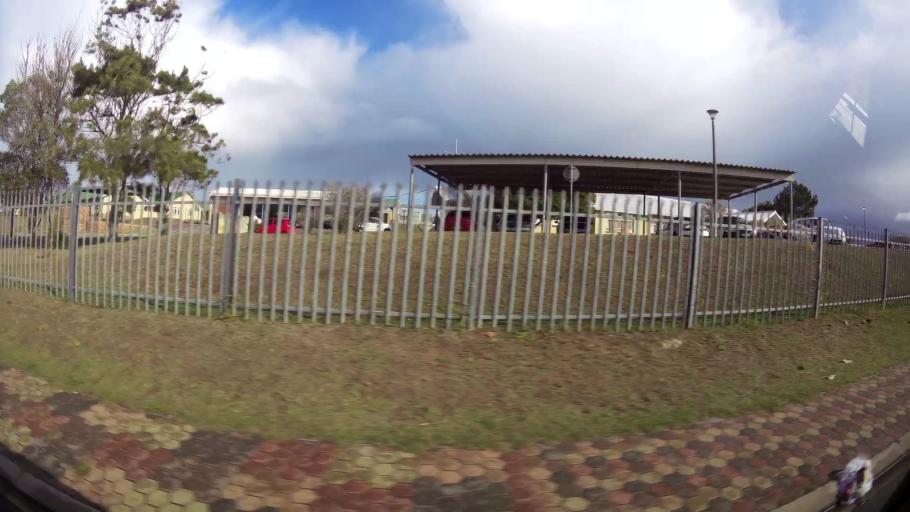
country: ZA
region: Western Cape
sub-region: Eden District Municipality
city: Mossel Bay
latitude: -34.1856
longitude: 22.1280
